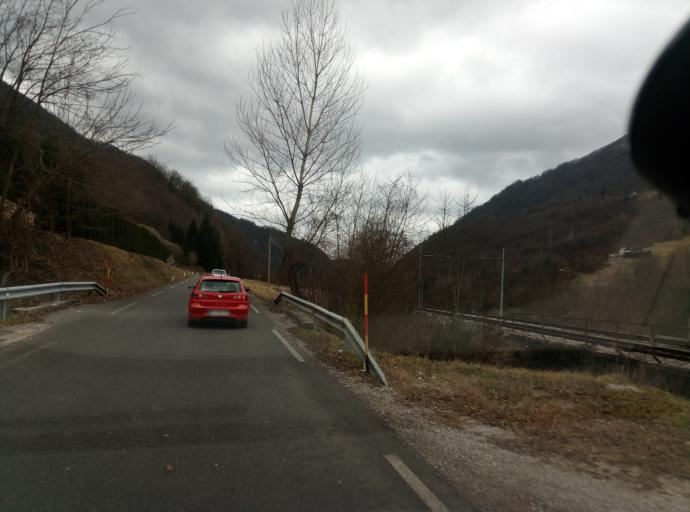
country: SI
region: Hrastnik
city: Dol pri Hrastniku
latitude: 46.1038
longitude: 15.1364
